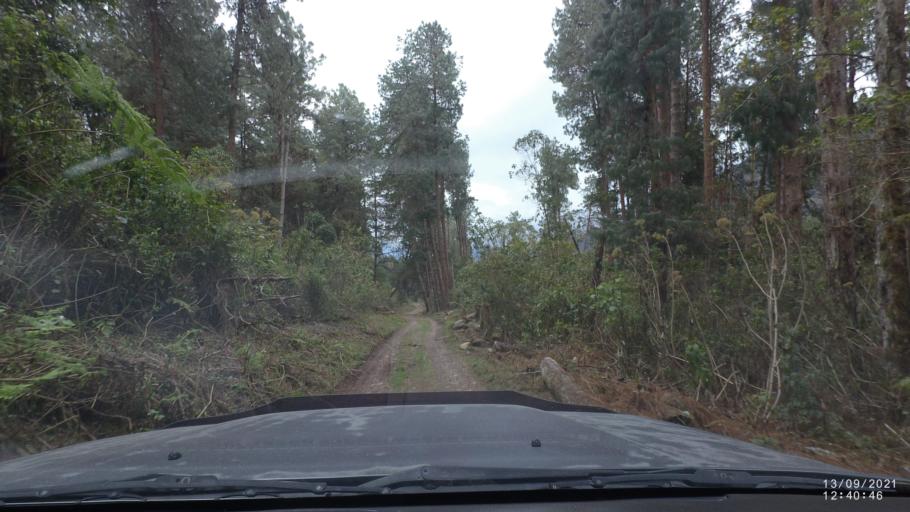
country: BO
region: Cochabamba
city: Colomi
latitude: -17.2582
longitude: -65.8157
